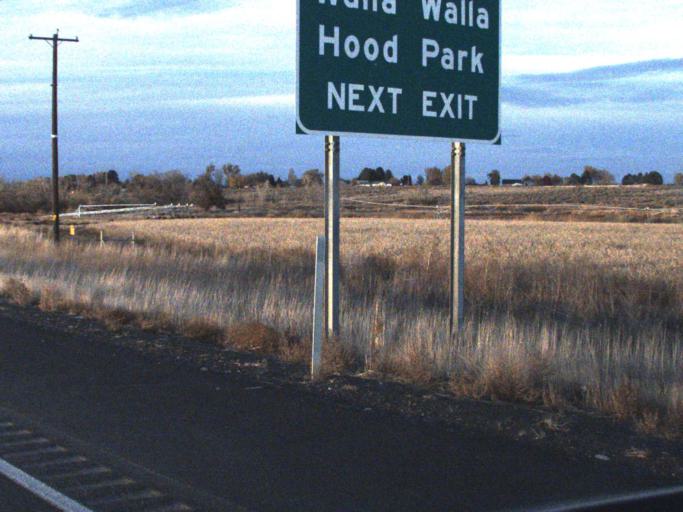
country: US
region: Washington
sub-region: Walla Walla County
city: Burbank
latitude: 46.2017
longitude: -119.0019
